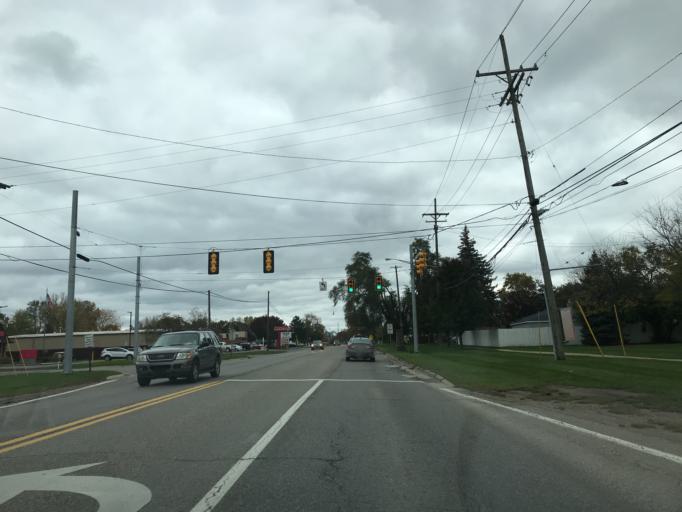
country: US
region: Michigan
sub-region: Oakland County
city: South Lyon
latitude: 42.4524
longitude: -83.6509
